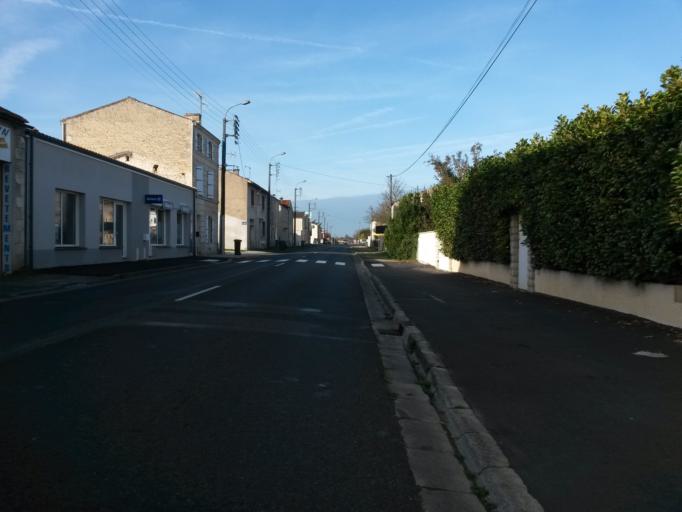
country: FR
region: Poitou-Charentes
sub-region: Departement des Deux-Sevres
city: Aiffres
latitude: 46.3170
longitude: -0.4322
